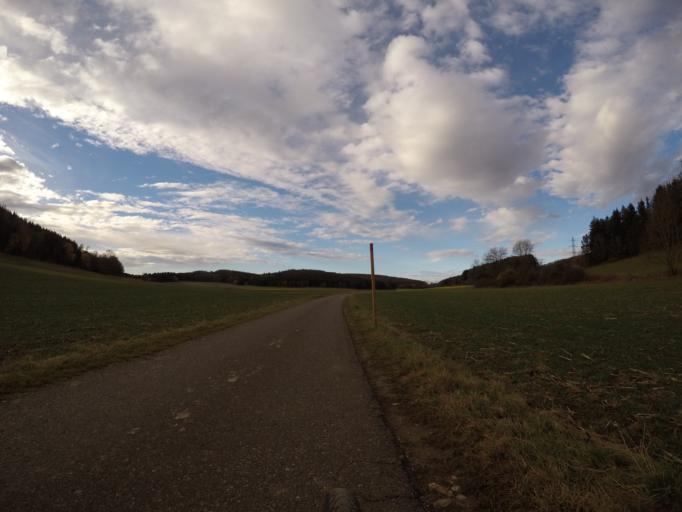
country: DE
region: Baden-Wuerttemberg
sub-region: Tuebingen Region
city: Sankt Johann
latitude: 48.4487
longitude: 9.3278
